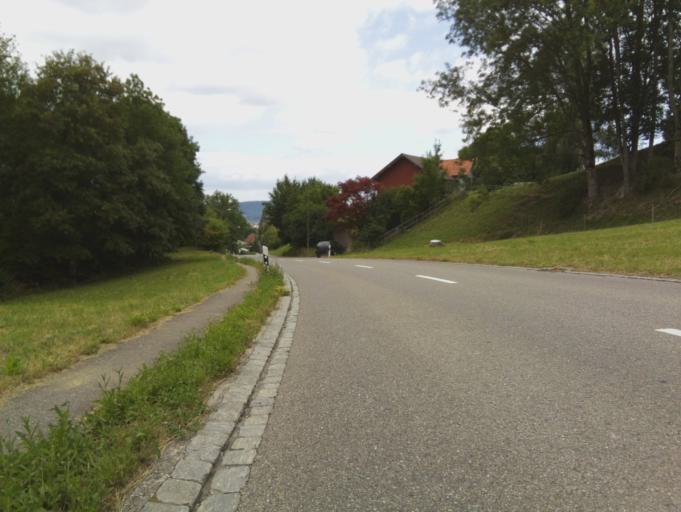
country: CH
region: Saint Gallen
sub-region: Wahlkreis Wil
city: Jonschwil
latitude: 47.4192
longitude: 9.0848
